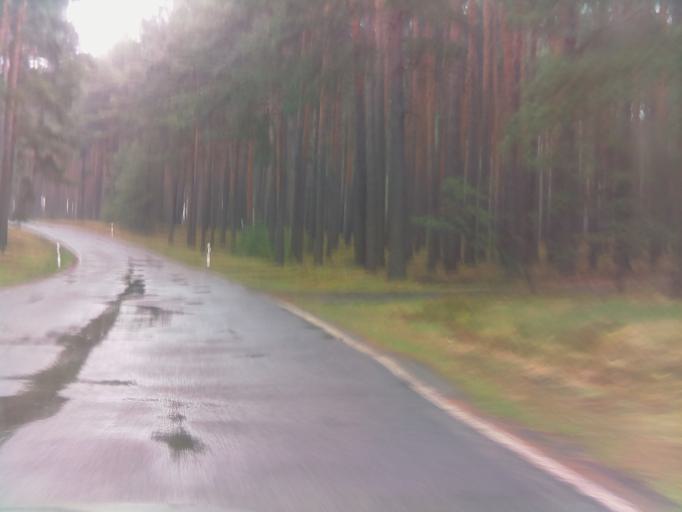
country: DE
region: Brandenburg
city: Jamlitz
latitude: 52.0349
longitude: 14.4010
